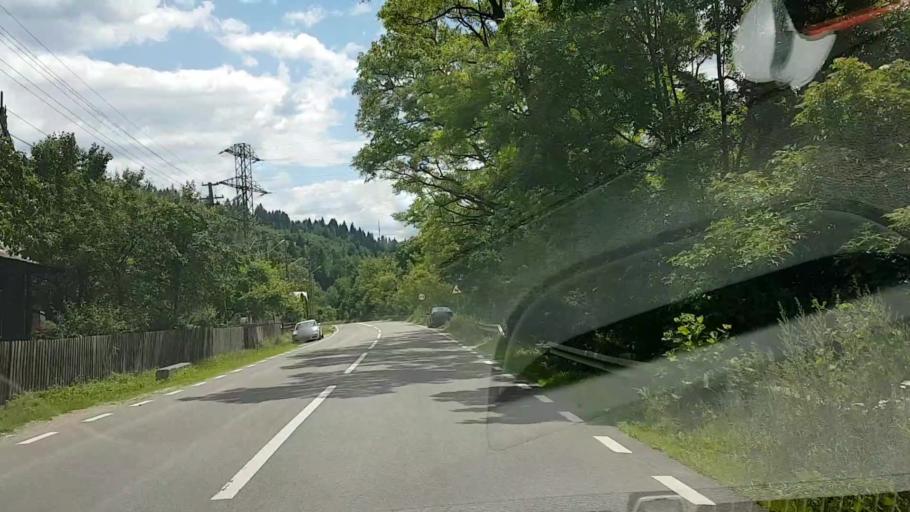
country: RO
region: Suceava
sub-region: Comuna Brosteni
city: Brosteni
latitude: 47.2566
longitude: 25.6917
